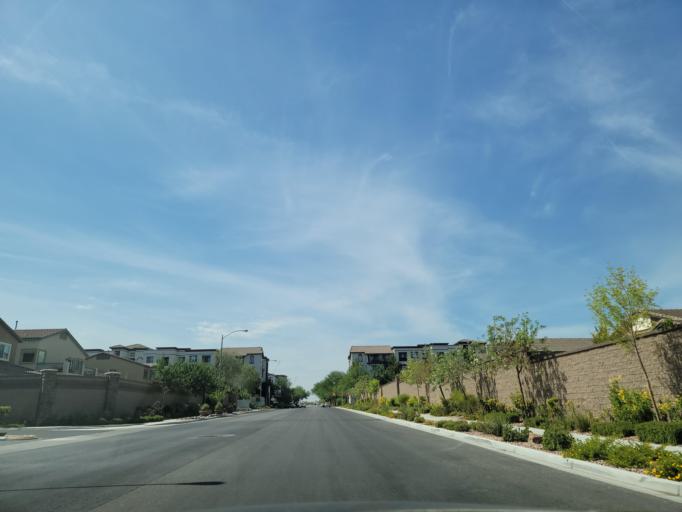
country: US
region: Nevada
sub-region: Clark County
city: Spring Valley
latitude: 36.0753
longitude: -115.2840
